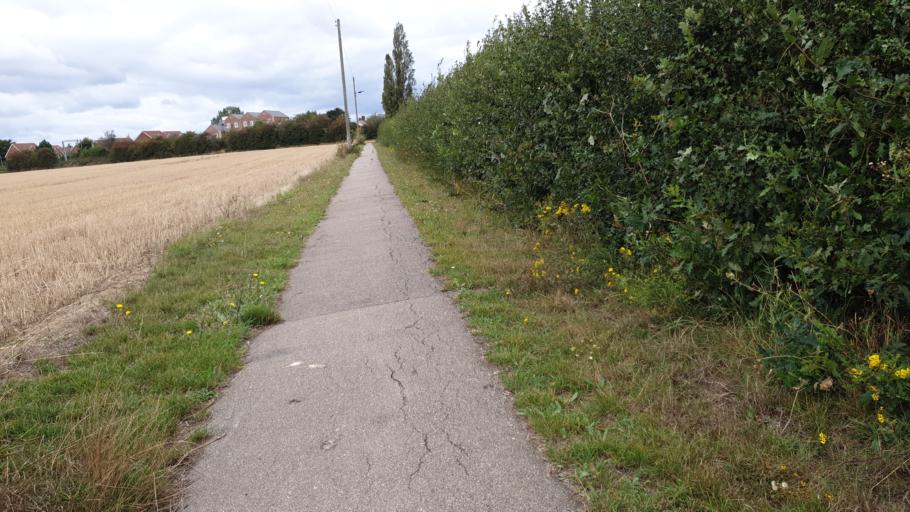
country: GB
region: England
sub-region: Essex
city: Frinton-on-Sea
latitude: 51.8396
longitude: 1.2156
